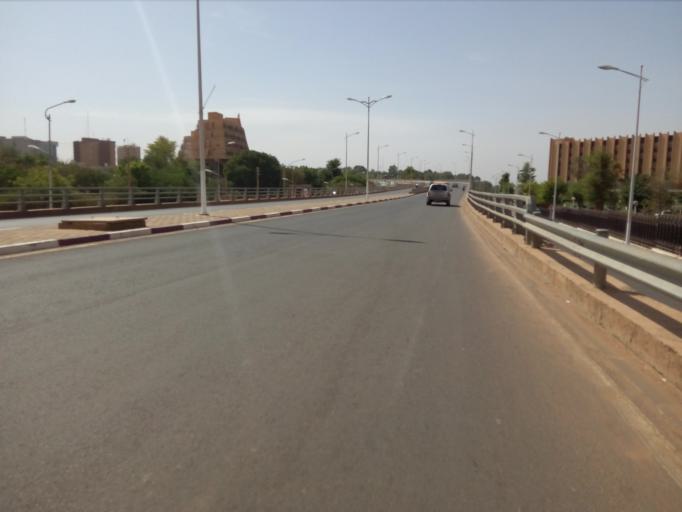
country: NE
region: Niamey
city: Niamey
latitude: 13.5108
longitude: 2.1056
